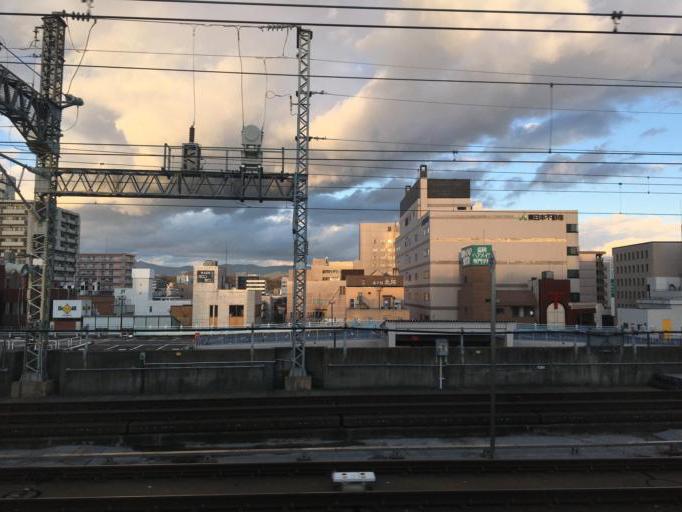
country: JP
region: Iwate
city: Morioka-shi
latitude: 39.7032
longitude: 141.1346
